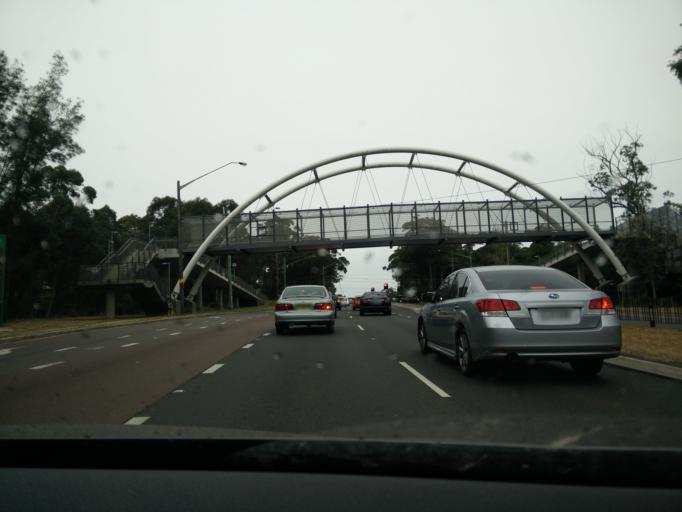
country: AU
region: New South Wales
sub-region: Ryde
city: Marsfield
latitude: -33.7717
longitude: 151.0998
